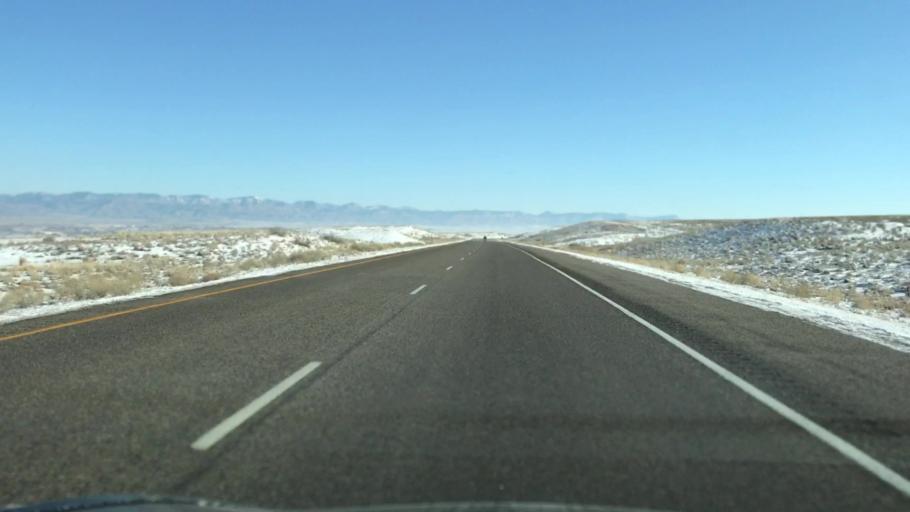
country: US
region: Colorado
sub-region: Mesa County
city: Loma
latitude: 39.2272
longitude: -108.9223
